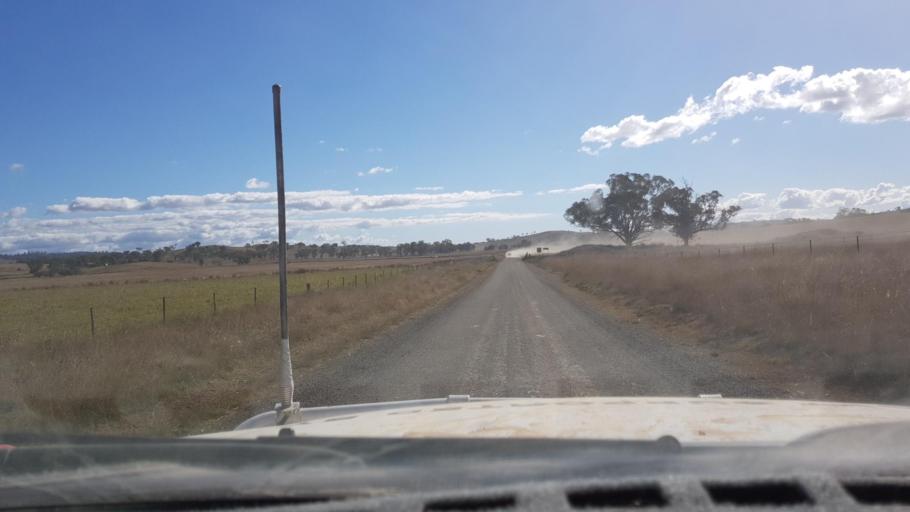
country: AU
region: New South Wales
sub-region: Narrabri
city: Blair Athol
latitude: -30.5140
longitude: 150.4446
